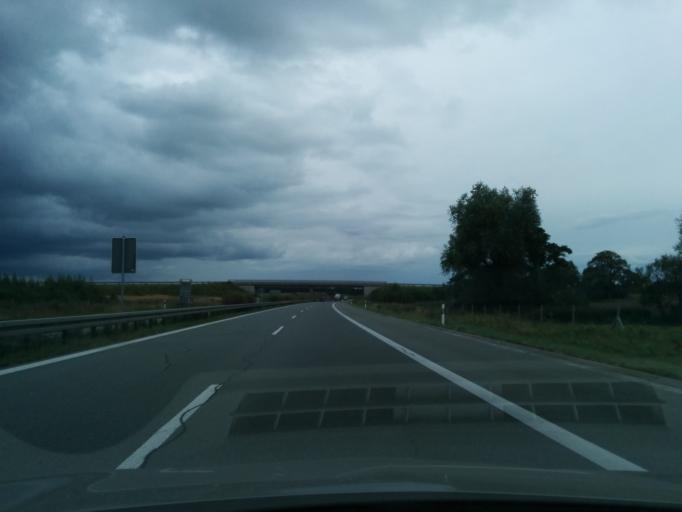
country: DE
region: Mecklenburg-Vorpommern
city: Brunn
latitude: 53.6538
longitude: 13.3649
